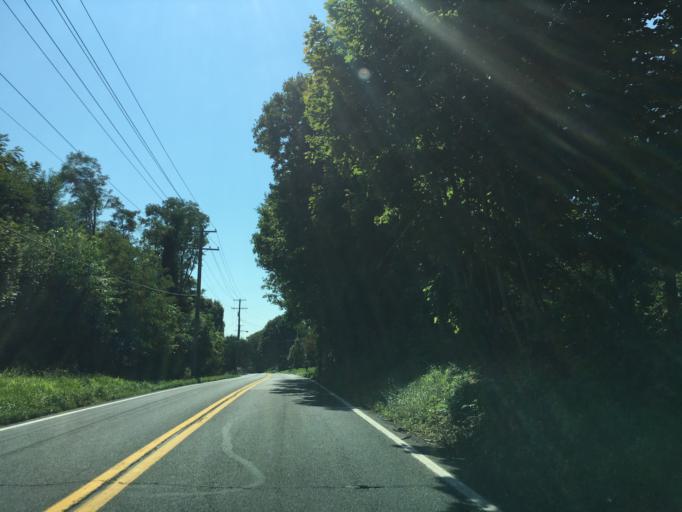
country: US
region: Pennsylvania
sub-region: York County
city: New Freedom
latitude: 39.6461
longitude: -76.6961
